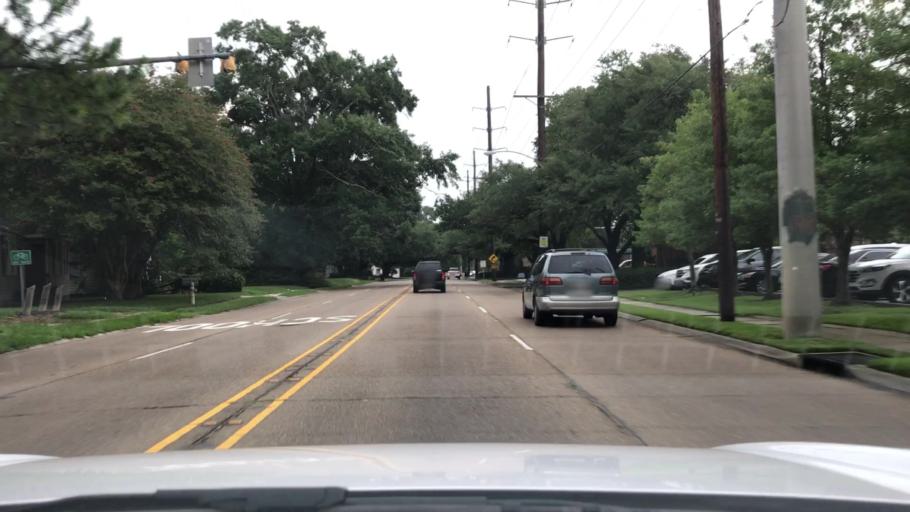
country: US
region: Louisiana
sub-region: East Baton Rouge Parish
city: Baton Rouge
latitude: 30.4326
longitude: -91.1349
